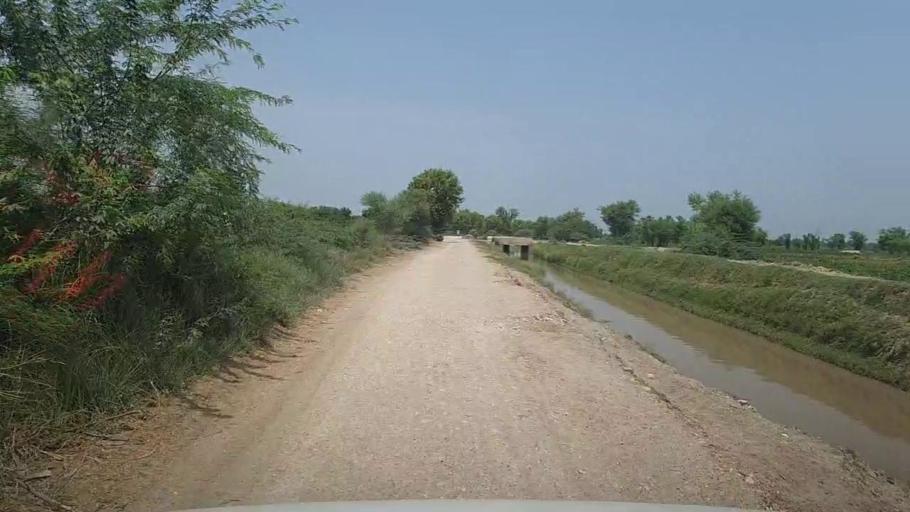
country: PK
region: Sindh
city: Karaundi
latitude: 26.9000
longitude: 68.3312
